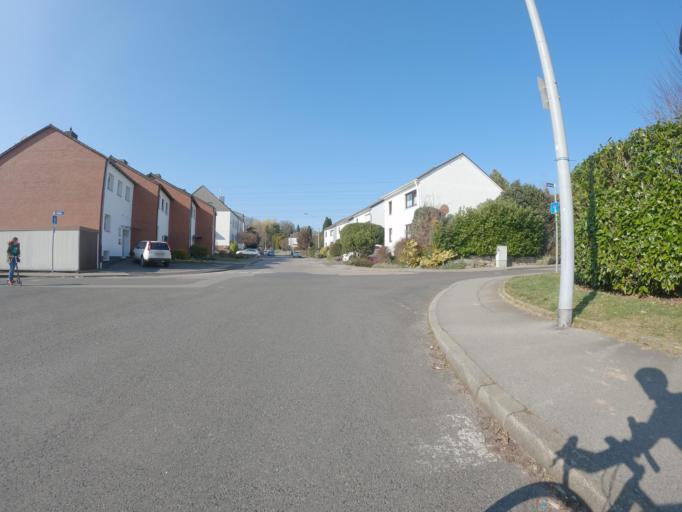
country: DE
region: North Rhine-Westphalia
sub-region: Regierungsbezirk Koln
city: Wurselen
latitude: 50.7997
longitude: 6.1219
